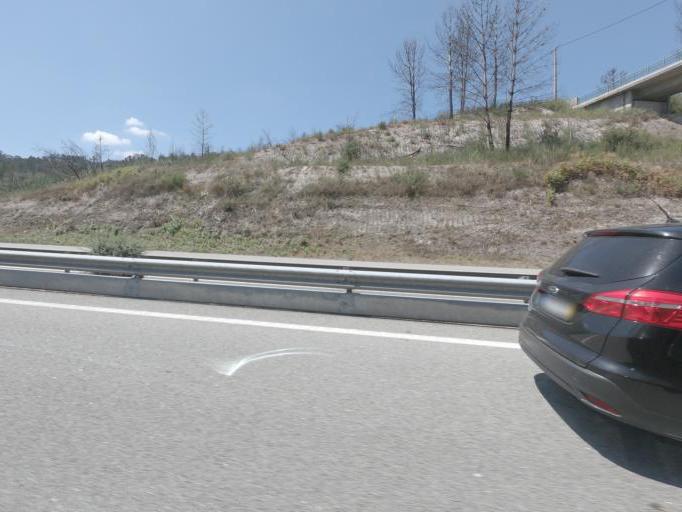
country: PT
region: Porto
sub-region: Amarante
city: Amarante
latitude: 41.2409
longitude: -8.1180
